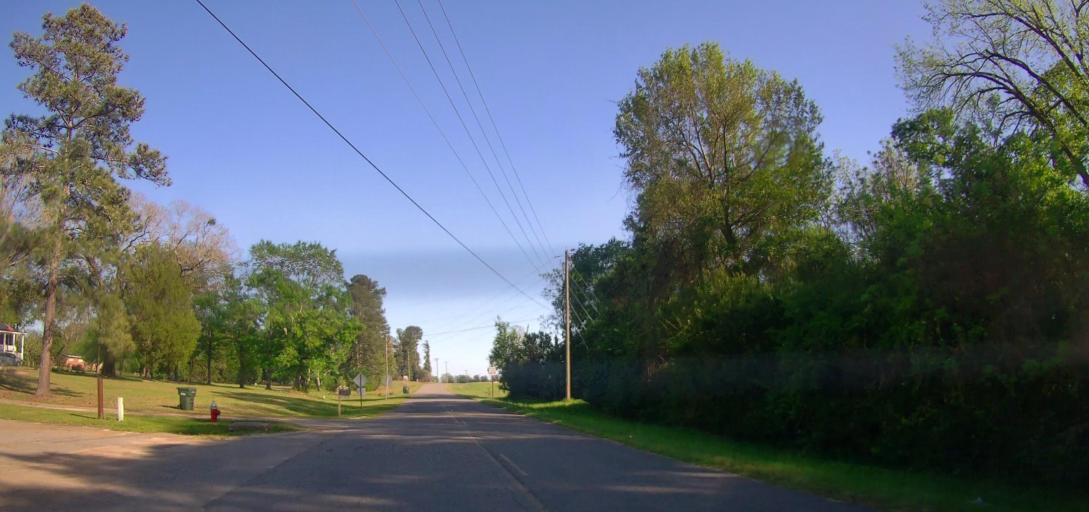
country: US
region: Georgia
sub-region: Houston County
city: Perry
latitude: 32.4392
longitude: -83.7883
